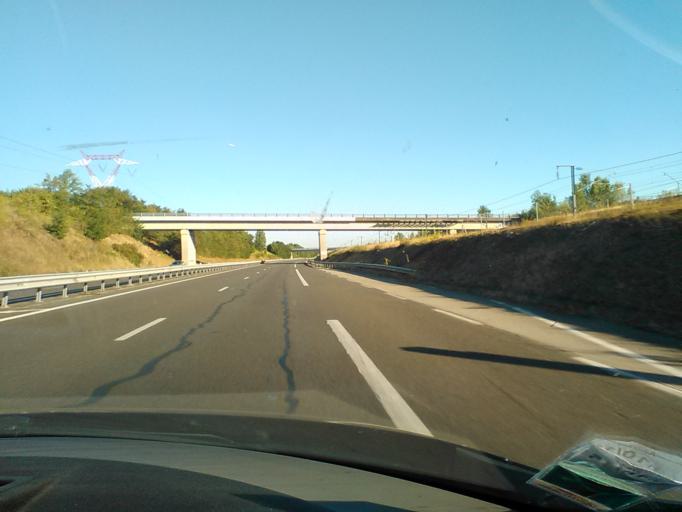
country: FR
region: Rhone-Alpes
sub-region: Departement du Rhone
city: Jons
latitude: 45.8051
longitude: 5.0681
